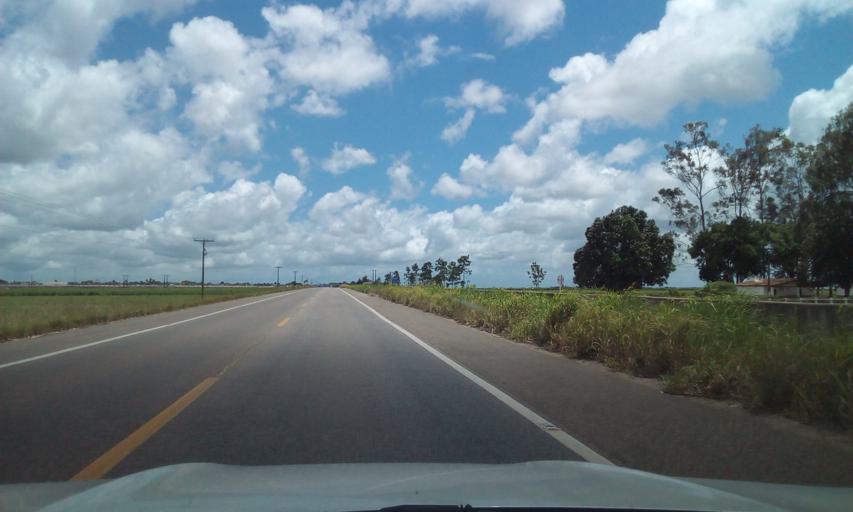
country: BR
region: Alagoas
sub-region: Campo Alegre
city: Campo Alegre
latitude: -9.9020
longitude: -36.2368
